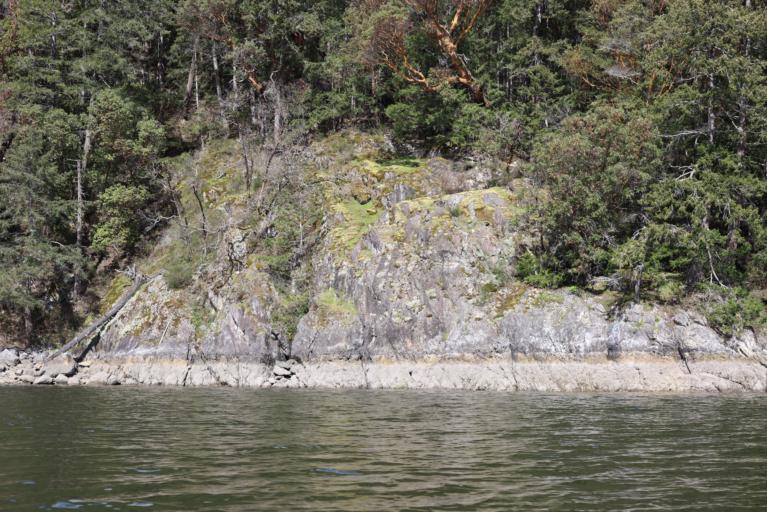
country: CA
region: British Columbia
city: Langford
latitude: 48.5607
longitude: -123.5316
